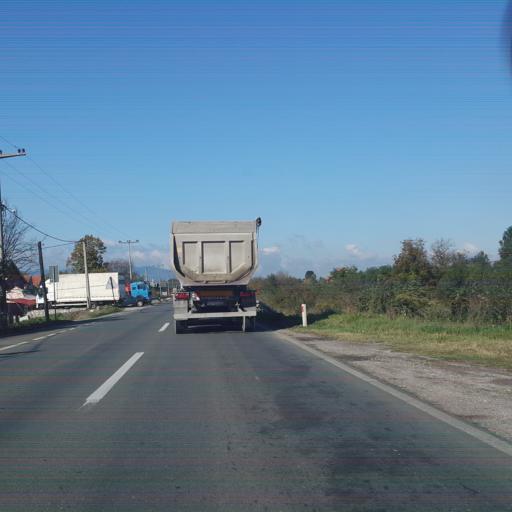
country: RS
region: Central Serbia
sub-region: Rasinski Okrug
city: Trstenik
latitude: 43.6334
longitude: 20.9532
